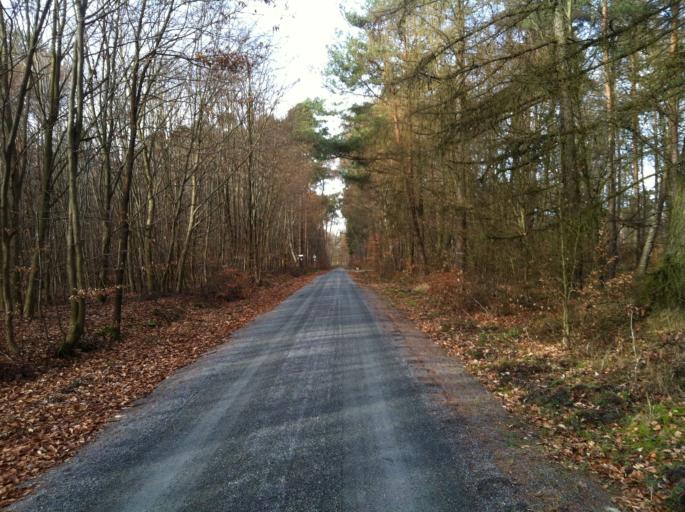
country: DE
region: Hesse
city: Morfelden-Walldorf
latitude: 50.0275
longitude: 8.6266
